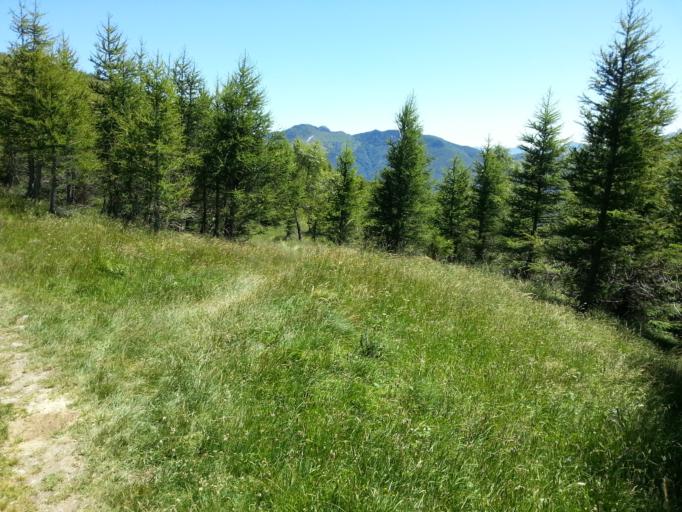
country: CH
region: Ticino
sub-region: Bellinzona District
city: Camorino
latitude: 46.1088
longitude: 9.0338
